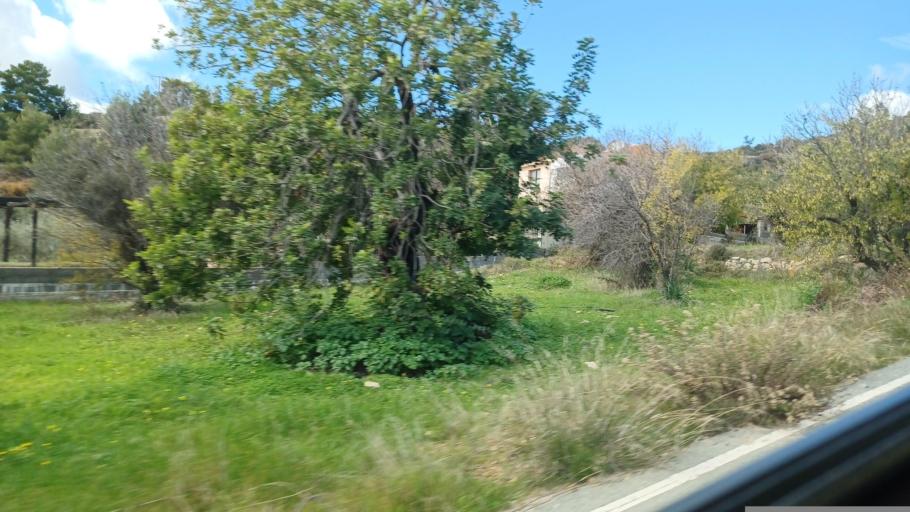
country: CY
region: Limassol
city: Pano Polemidia
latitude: 34.7926
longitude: 32.9782
